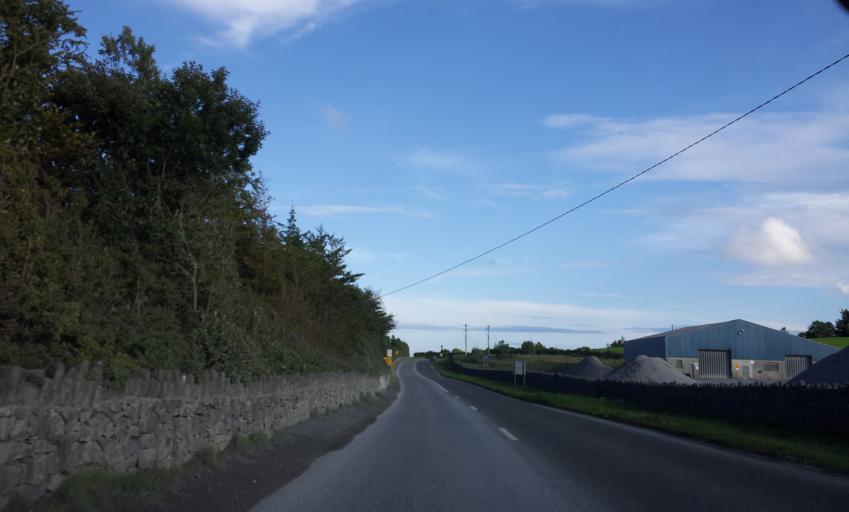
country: IE
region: Munster
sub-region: An Clar
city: Ennis
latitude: 52.9005
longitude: -9.0349
